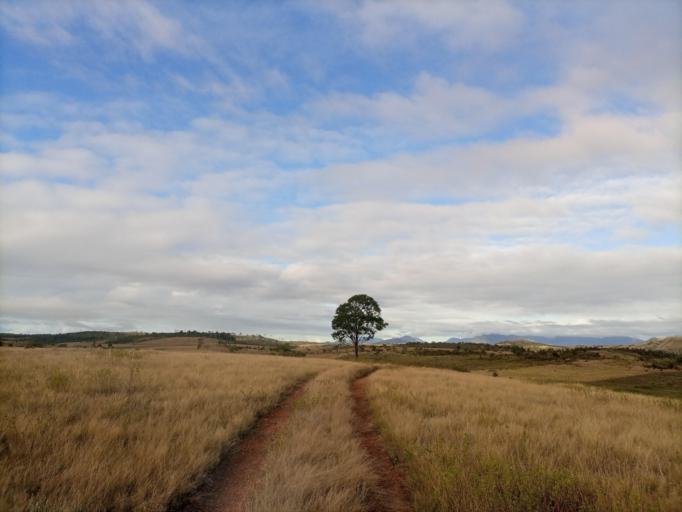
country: MG
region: Anosy
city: Fort Dauphin
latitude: -24.3135
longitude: 47.2600
